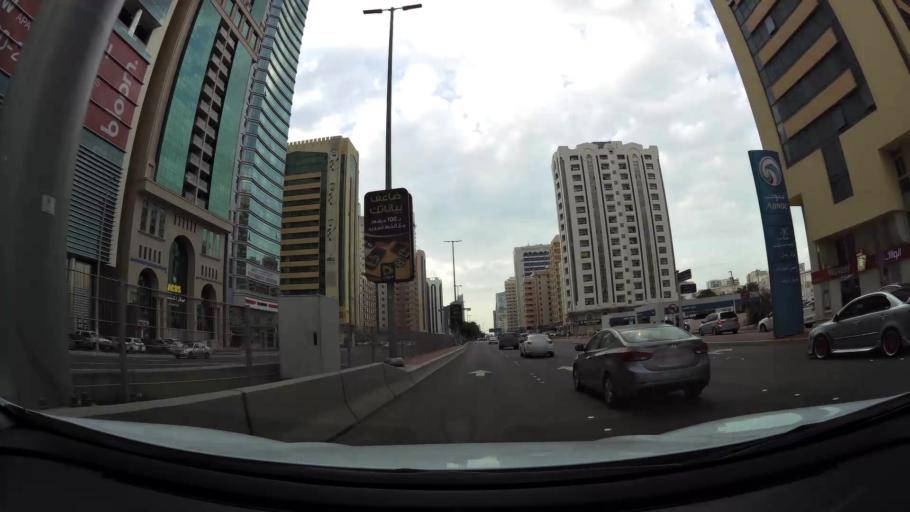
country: AE
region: Abu Dhabi
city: Abu Dhabi
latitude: 24.4712
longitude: 54.3699
